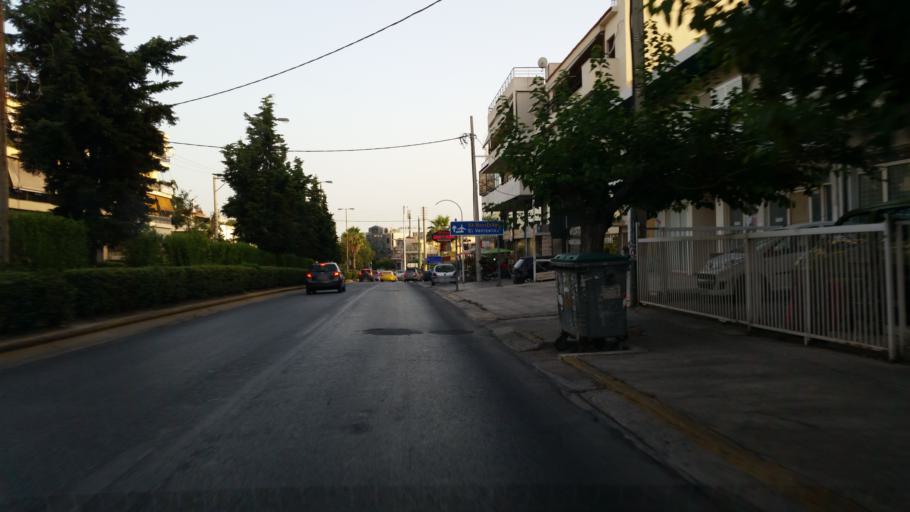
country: GR
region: Attica
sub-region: Nomarchia Athinas
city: Argyroupoli
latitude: 37.9071
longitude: 23.7540
